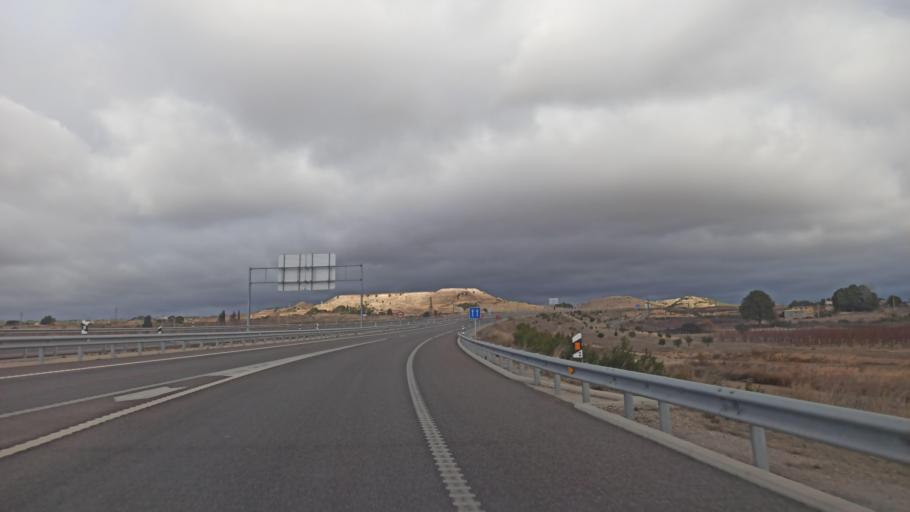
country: ES
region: Catalonia
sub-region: Provincia de Lleida
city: Torrefarrera
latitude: 41.6599
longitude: 0.5828
